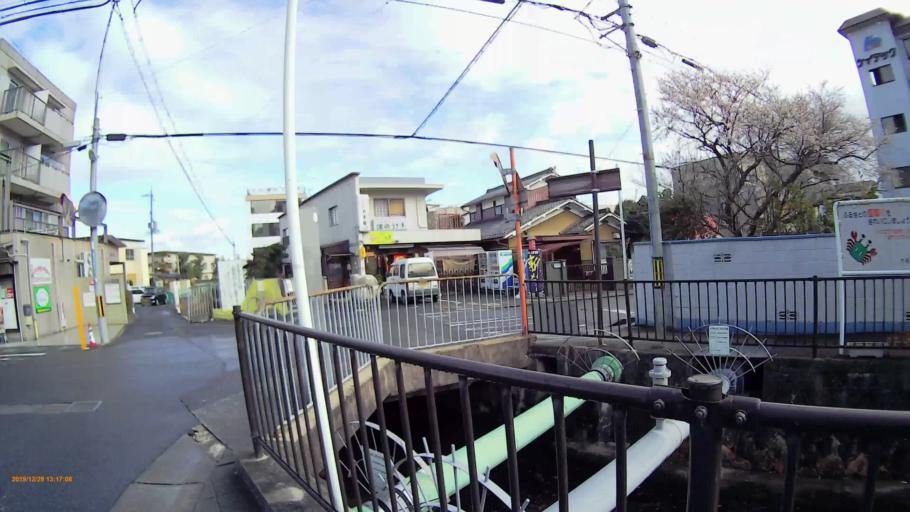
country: JP
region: Shiga Prefecture
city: Otsu-shi
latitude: 34.9815
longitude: 135.9013
